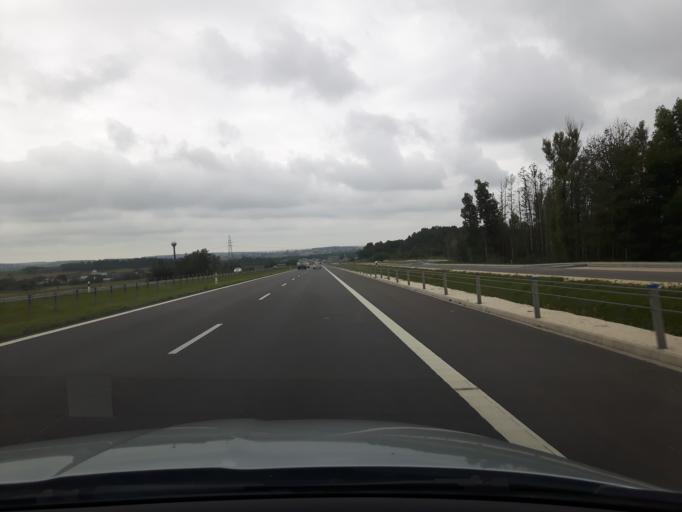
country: PL
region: Swietokrzyskie
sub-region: Powiat kielecki
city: Checiny
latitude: 50.7888
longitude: 20.4746
